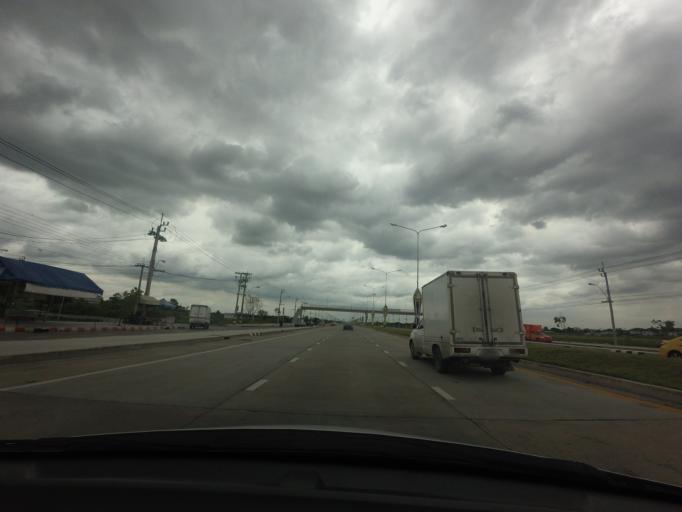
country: TH
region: Bangkok
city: Saphan Sung
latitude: 13.7550
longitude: 100.7282
